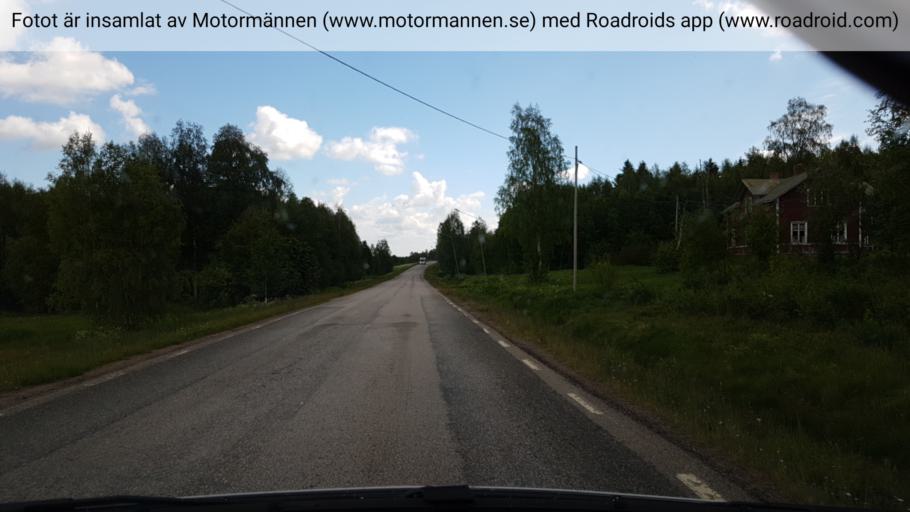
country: FI
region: Lapland
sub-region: Torniolaakso
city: Ylitornio
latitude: 66.1859
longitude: 23.7579
